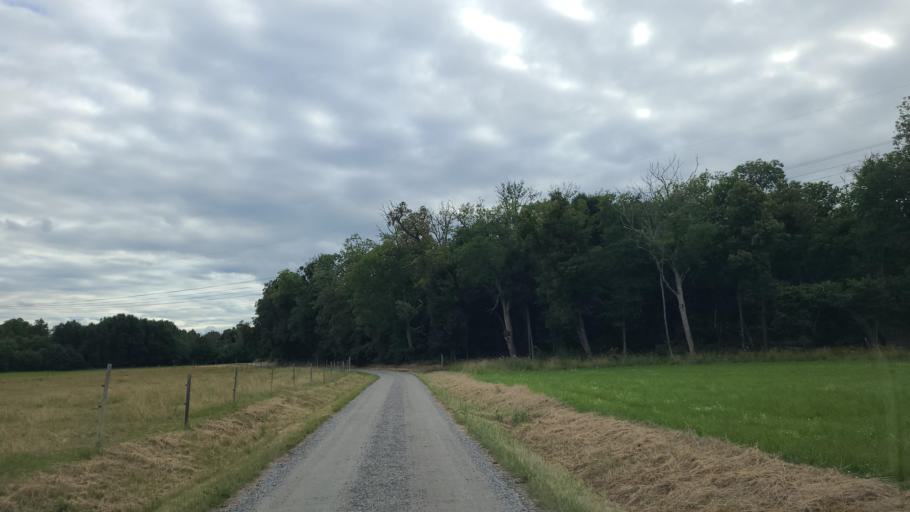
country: SE
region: Stockholm
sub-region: Upplands-Bro Kommun
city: Bro
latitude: 59.4602
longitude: 17.5832
